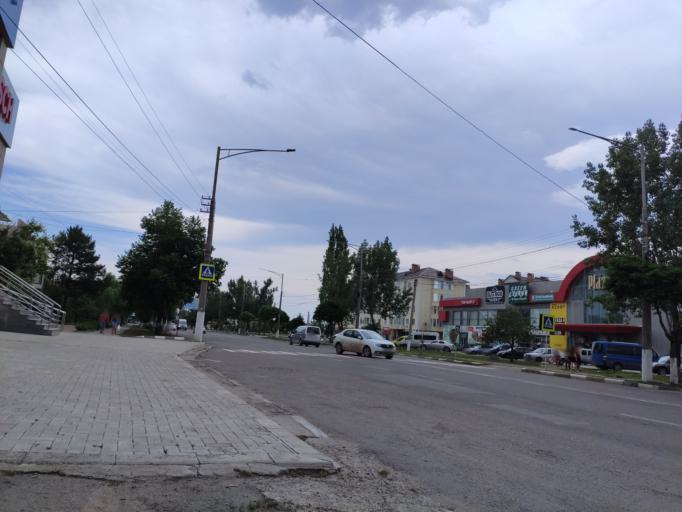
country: MD
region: Balti
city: Balti
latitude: 47.7630
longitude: 27.9410
